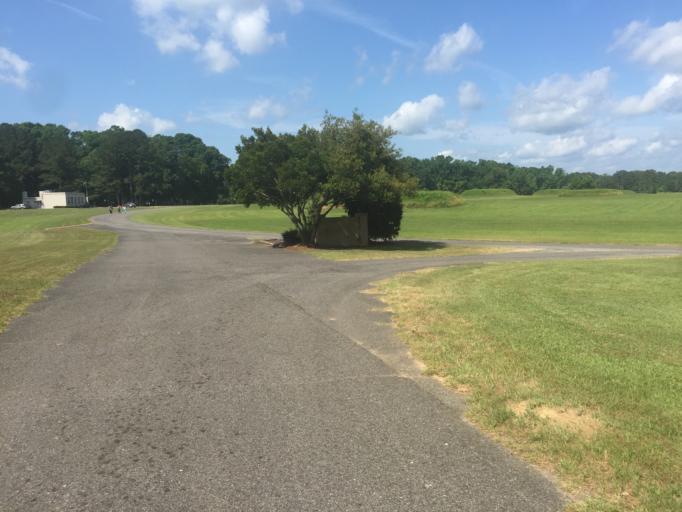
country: US
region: Alabama
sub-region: Hale County
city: Moundville
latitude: 33.0044
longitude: -87.6270
